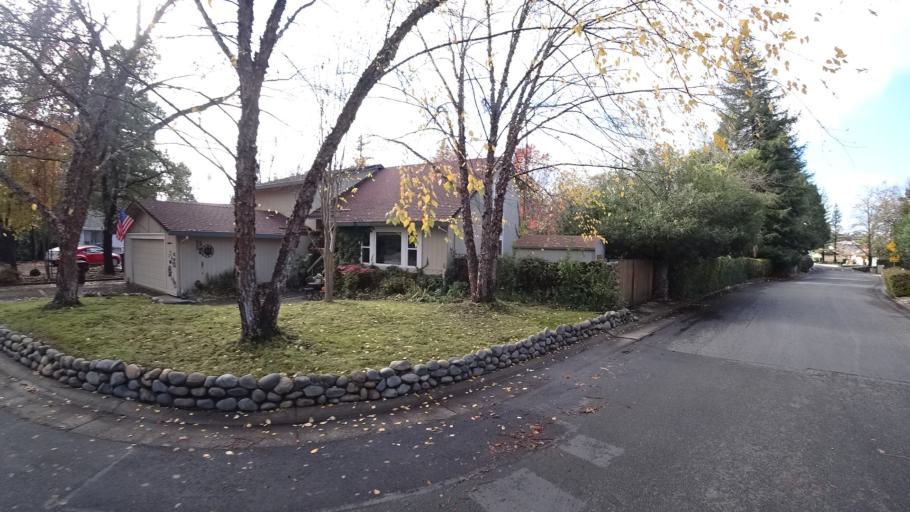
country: US
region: California
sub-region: Sacramento County
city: Antelope
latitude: 38.6851
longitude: -121.3233
